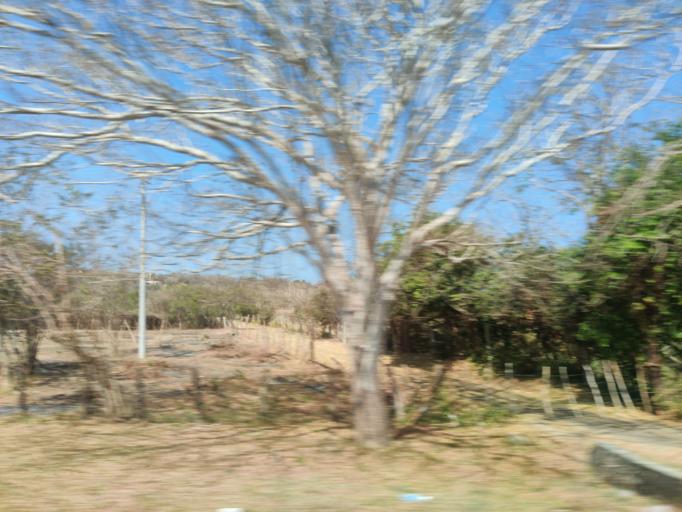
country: CO
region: Atlantico
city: Juan de Acosta
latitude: 10.8506
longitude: -75.1281
